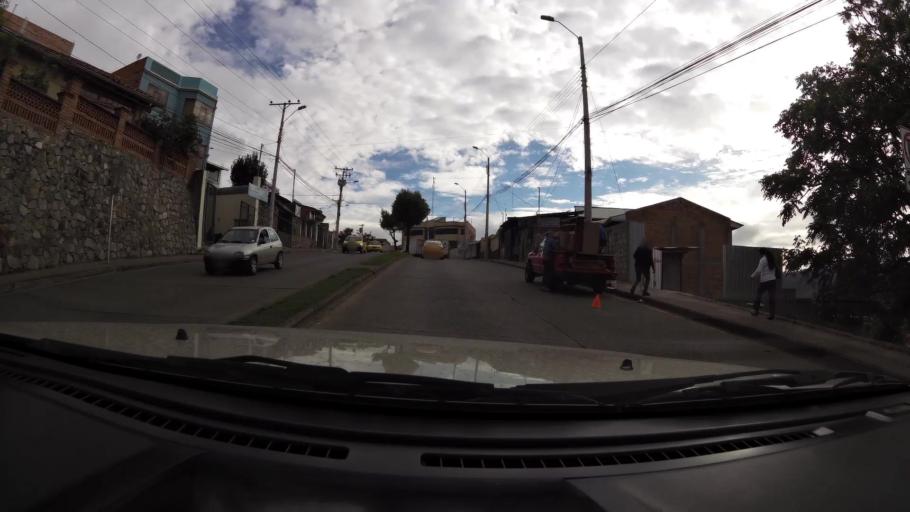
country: EC
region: Azuay
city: Cuenca
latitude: -2.8976
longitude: -78.9839
